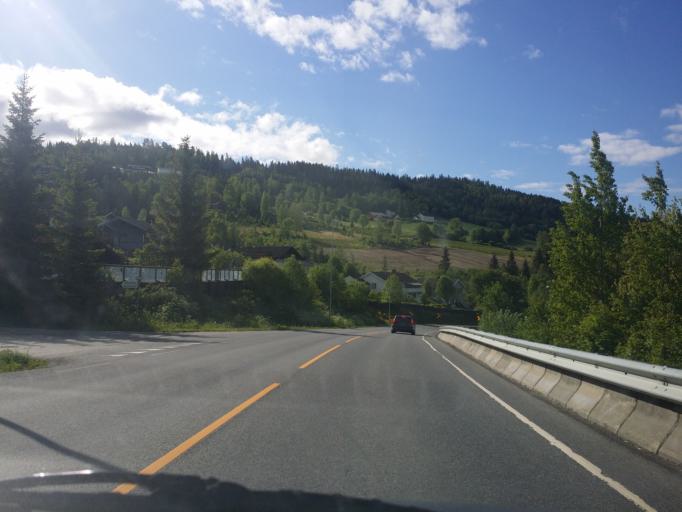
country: NO
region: Oppland
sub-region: Lillehammer
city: Lillehammer
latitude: 61.1026
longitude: 10.4917
